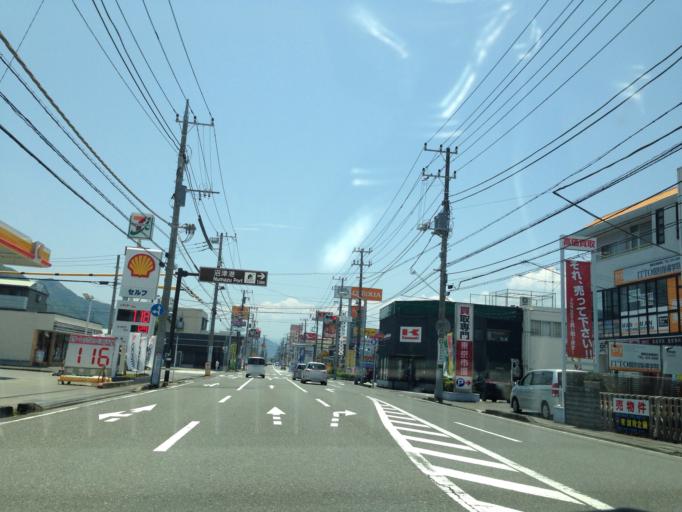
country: JP
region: Shizuoka
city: Numazu
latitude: 35.0867
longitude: 138.8677
